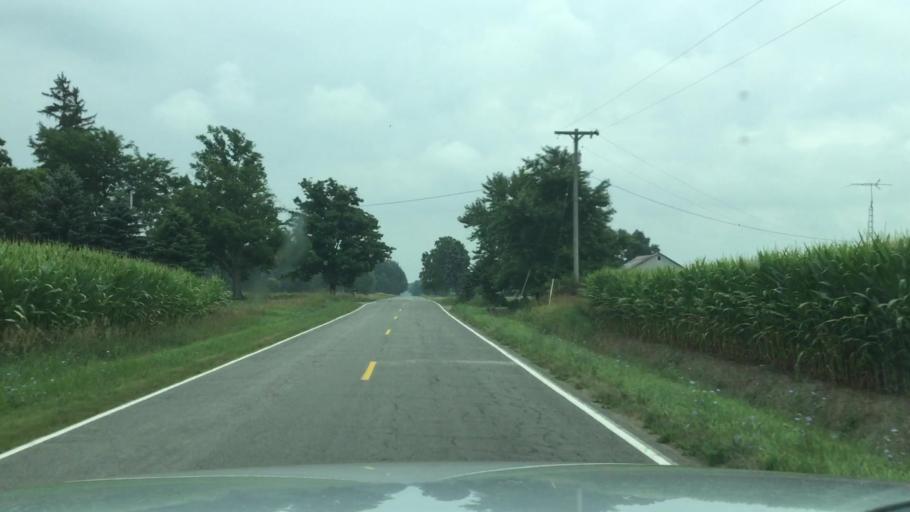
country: US
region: Michigan
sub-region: Shiawassee County
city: New Haven
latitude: 43.0826
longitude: -84.2261
